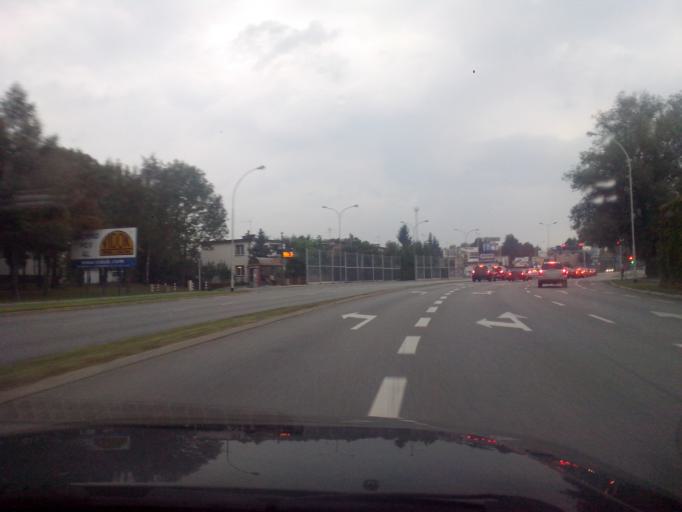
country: PL
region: Subcarpathian Voivodeship
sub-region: Rzeszow
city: Rzeszow
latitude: 50.0208
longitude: 21.9847
